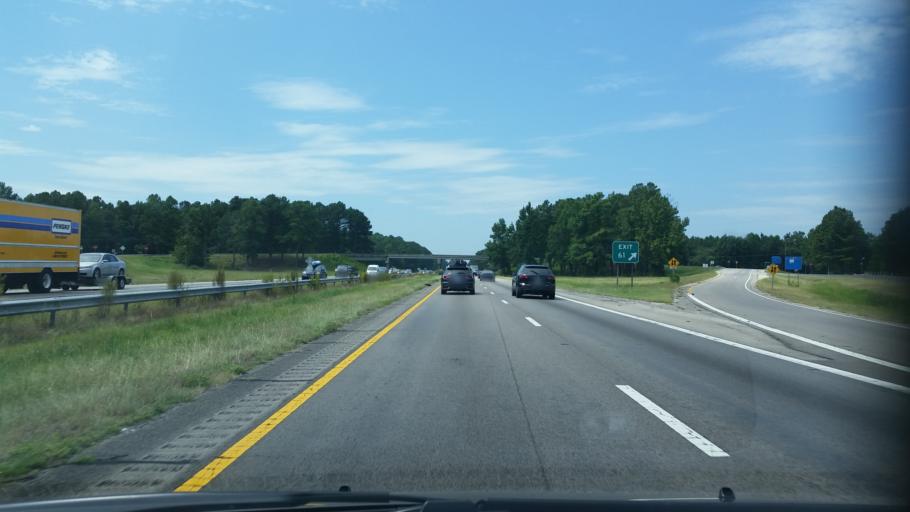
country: US
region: North Carolina
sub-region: Cumberland County
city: Eastover
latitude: 35.1611
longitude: -78.7143
